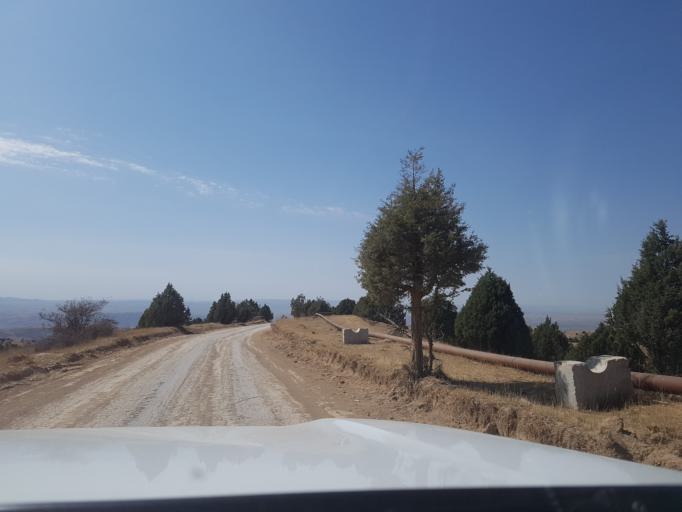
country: TM
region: Ahal
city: Baharly
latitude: 38.3144
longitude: 56.9521
